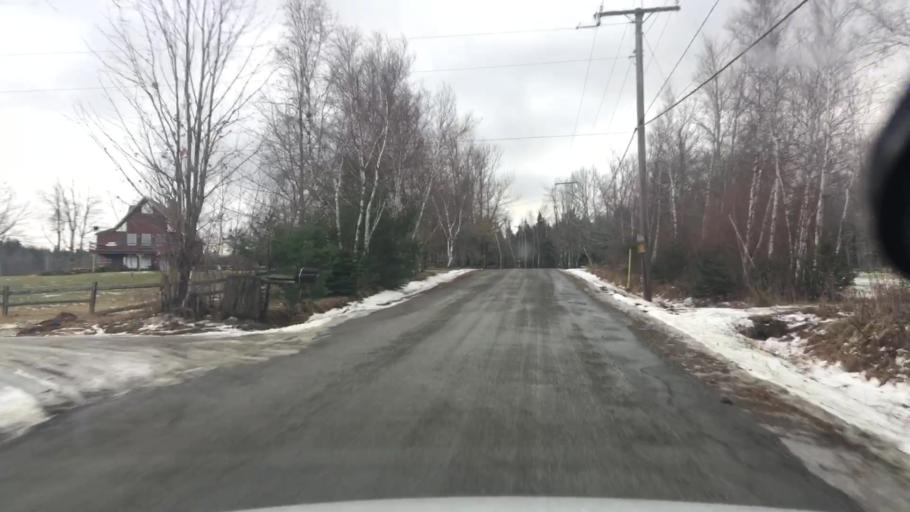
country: US
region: Maine
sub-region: Penobscot County
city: Orrington
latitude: 44.6805
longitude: -68.7556
